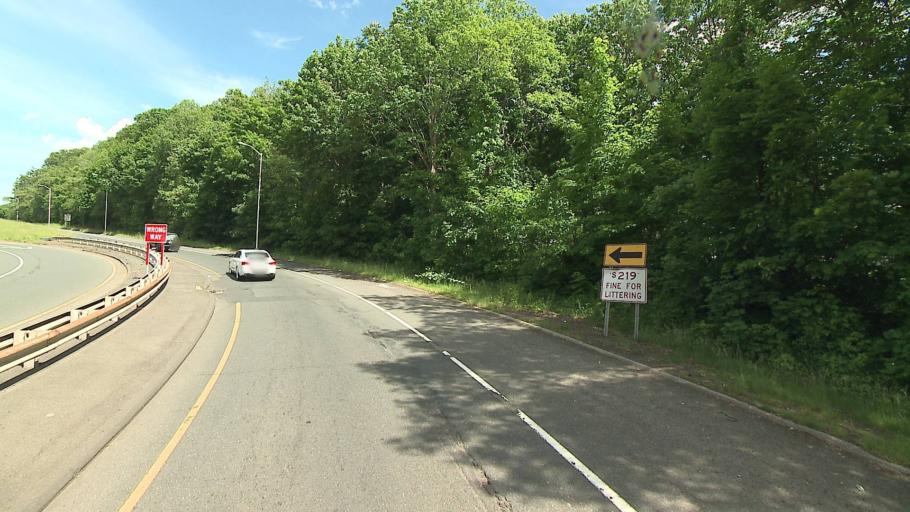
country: US
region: Connecticut
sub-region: New Haven County
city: Meriden
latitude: 41.5413
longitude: -72.7849
